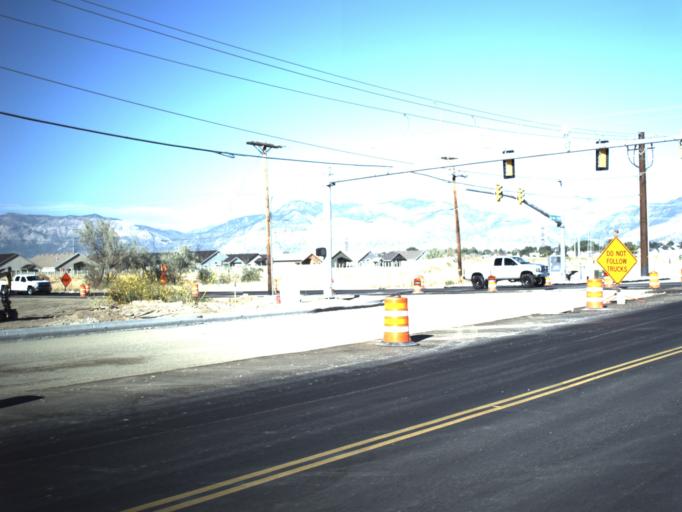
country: US
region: Utah
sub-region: Weber County
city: West Haven
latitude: 41.1906
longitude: -112.0650
